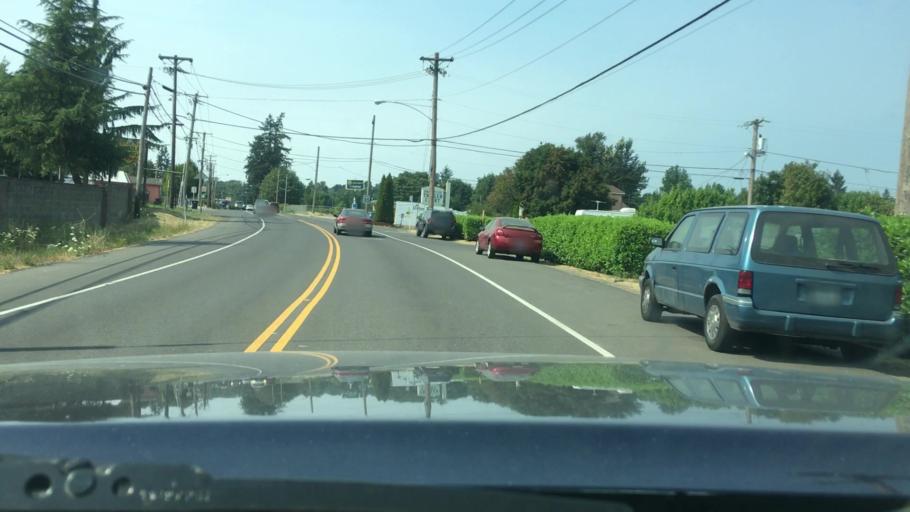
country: US
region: Oregon
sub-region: Lane County
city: Springfield
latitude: 44.0373
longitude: -123.0272
